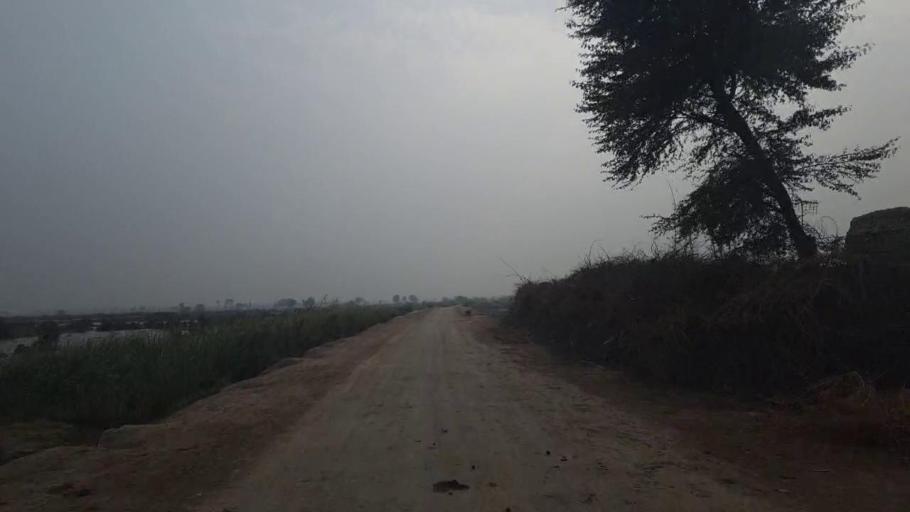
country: PK
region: Sindh
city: Tando Adam
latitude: 25.7869
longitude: 68.7086
